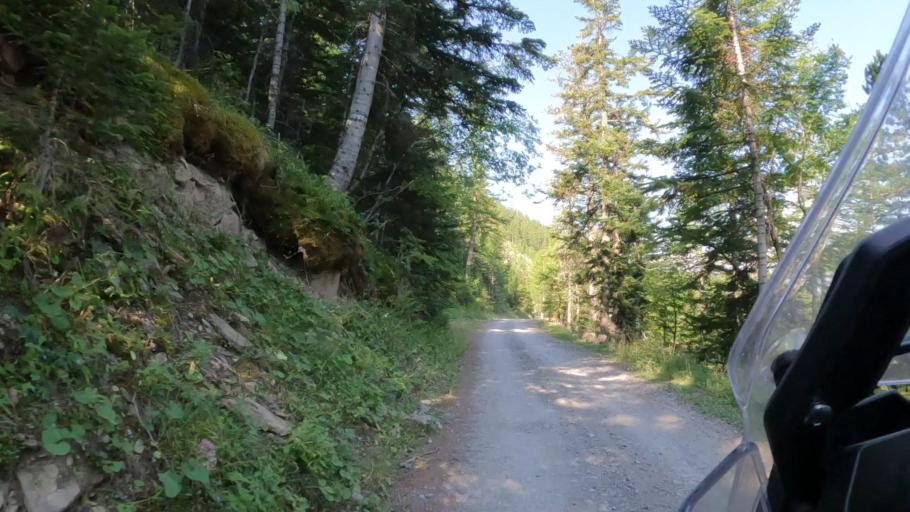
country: FR
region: Provence-Alpes-Cote d'Azur
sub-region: Departement des Hautes-Alpes
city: Embrun
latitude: 44.5913
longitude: 6.5795
